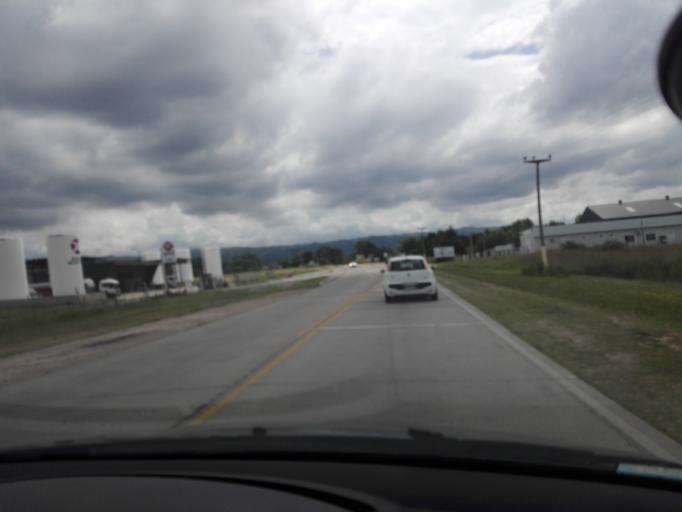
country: AR
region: Cordoba
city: Alta Gracia
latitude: -31.6347
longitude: -64.4328
